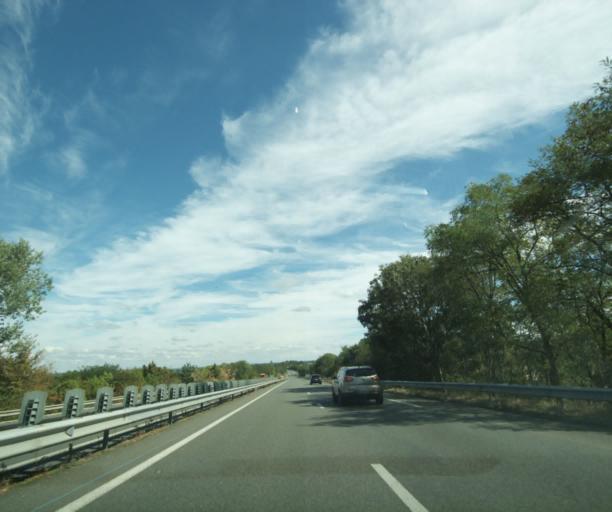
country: FR
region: Midi-Pyrenees
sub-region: Departement du Tarn-et-Garonne
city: Auvillar
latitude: 44.0591
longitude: 0.9114
